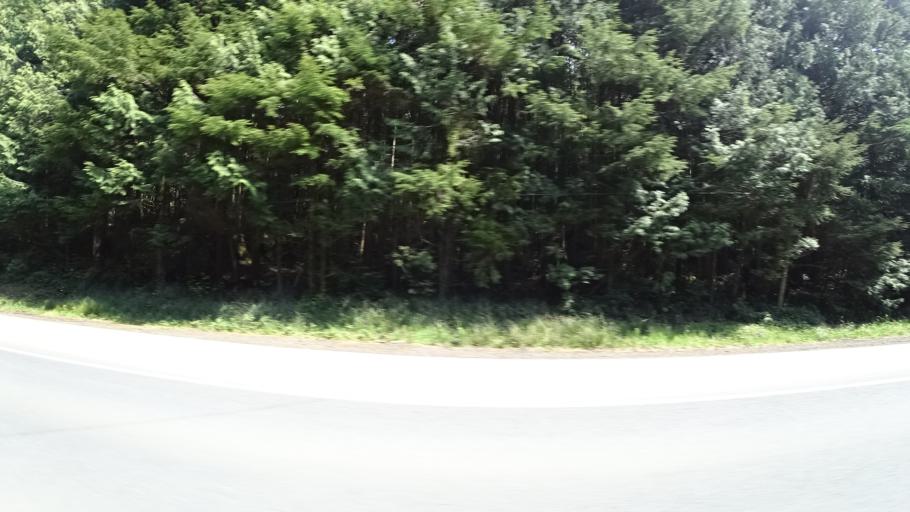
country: US
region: Oregon
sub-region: Lincoln County
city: Lincoln Beach
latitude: 44.8333
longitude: -124.0554
